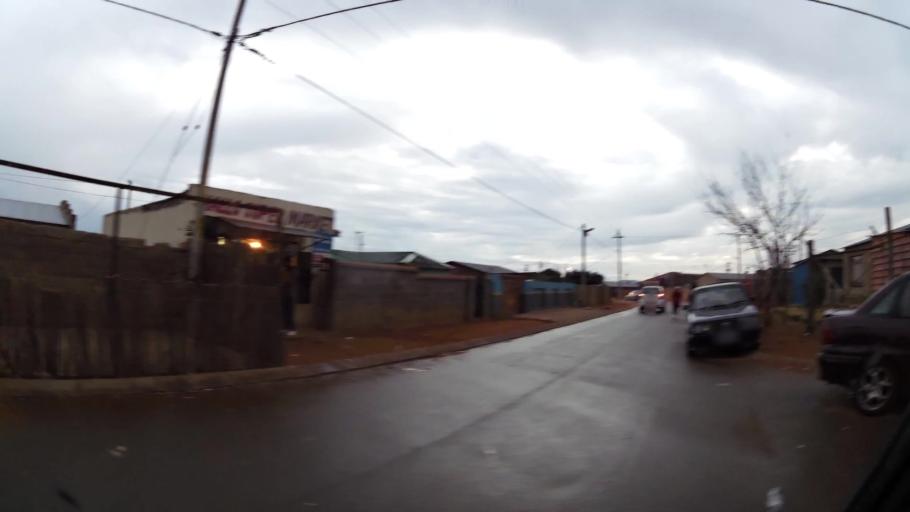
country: ZA
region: Gauteng
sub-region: West Rand District Municipality
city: Randfontein
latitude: -26.1774
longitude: 27.7848
